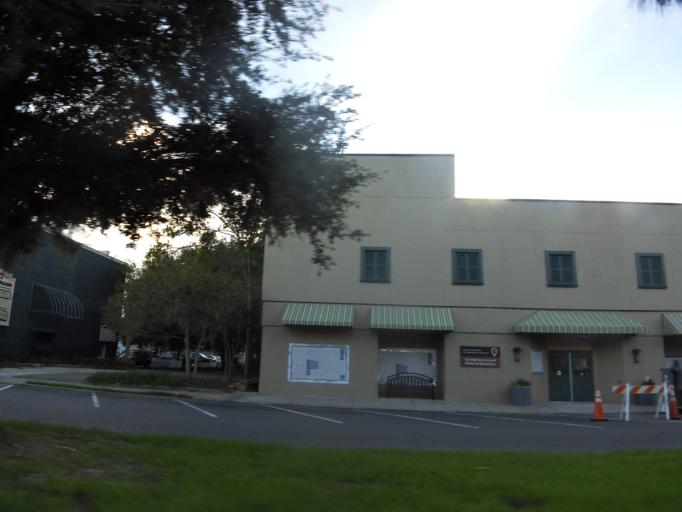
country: US
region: Georgia
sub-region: Camden County
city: St. Marys
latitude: 30.7213
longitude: -81.5484
